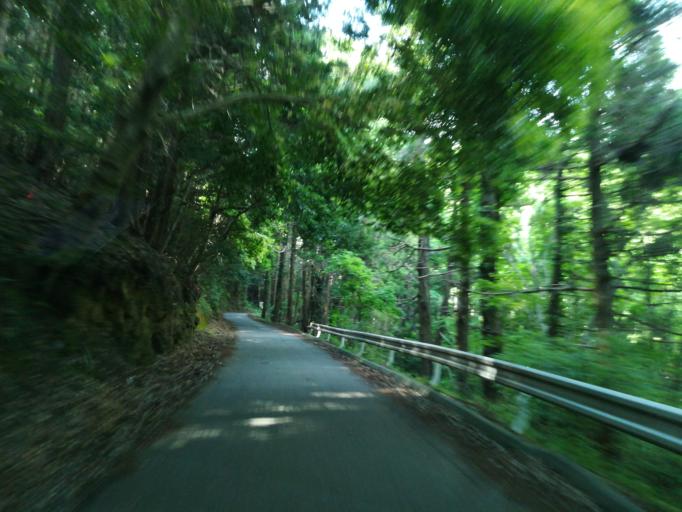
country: JP
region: Ibaraki
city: Tsukuba
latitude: 36.1840
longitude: 140.1181
